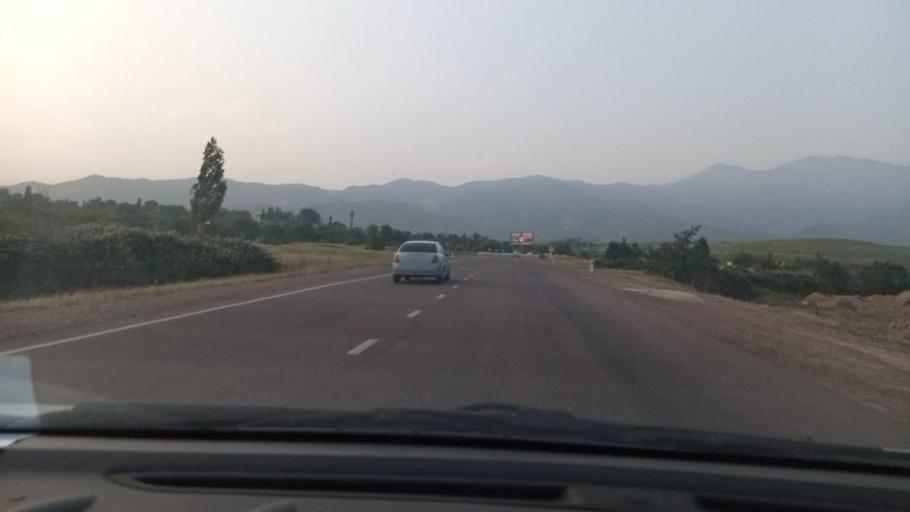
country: UZ
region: Toshkent
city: Angren
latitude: 41.0474
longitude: 70.1587
